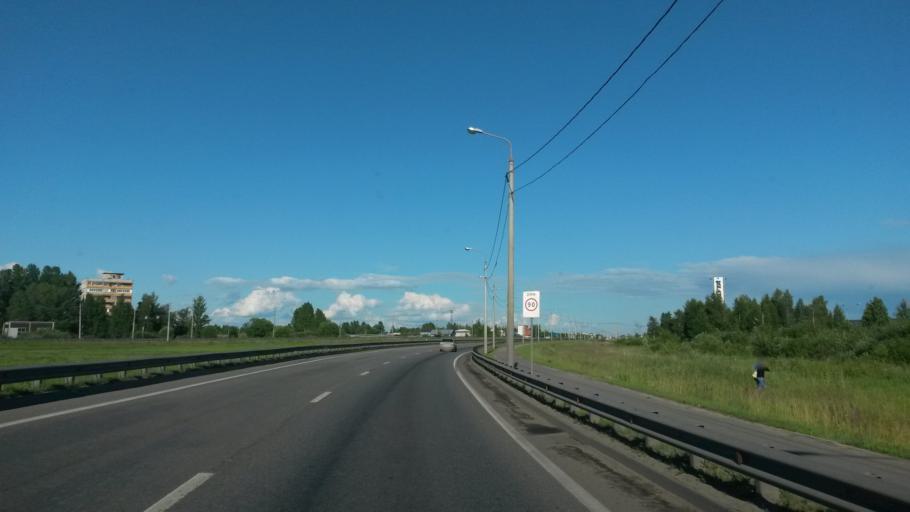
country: RU
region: Jaroslavl
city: Yaroslavl
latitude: 57.6700
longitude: 39.7745
